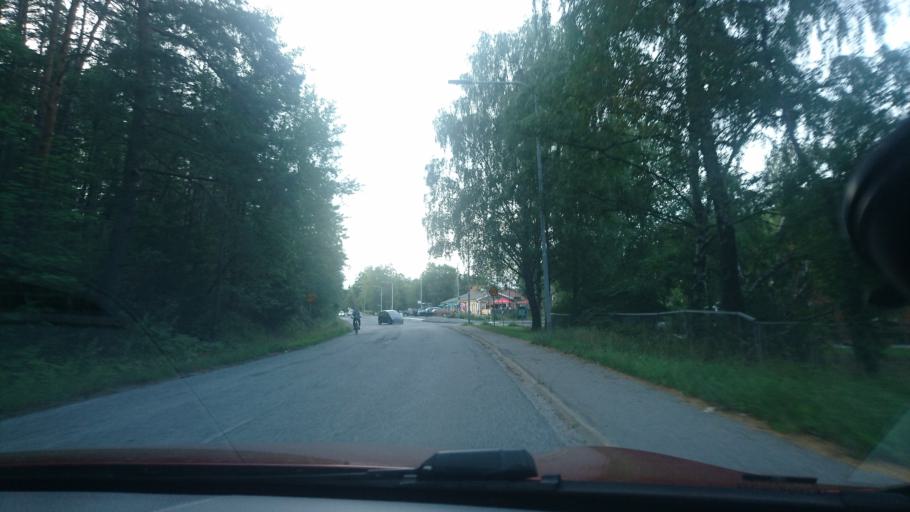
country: SE
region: Stockholm
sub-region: Sodertalje Kommun
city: Pershagen
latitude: 59.1528
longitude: 17.6499
